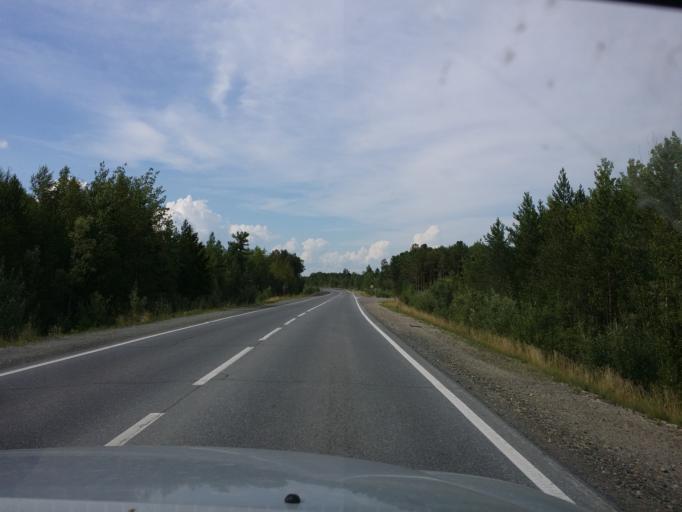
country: RU
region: Khanty-Mansiyskiy Avtonomnyy Okrug
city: Megion
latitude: 61.1144
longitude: 75.8414
